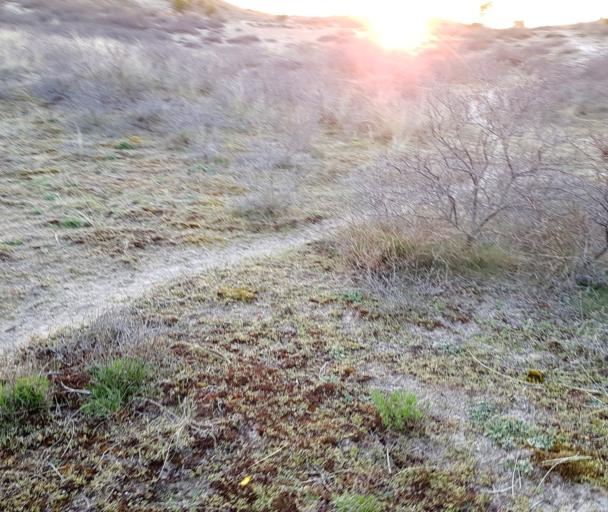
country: NL
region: South Holland
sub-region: Gemeente Noordwijkerhout
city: Noordwijkerhout
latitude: 52.3044
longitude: 4.4886
